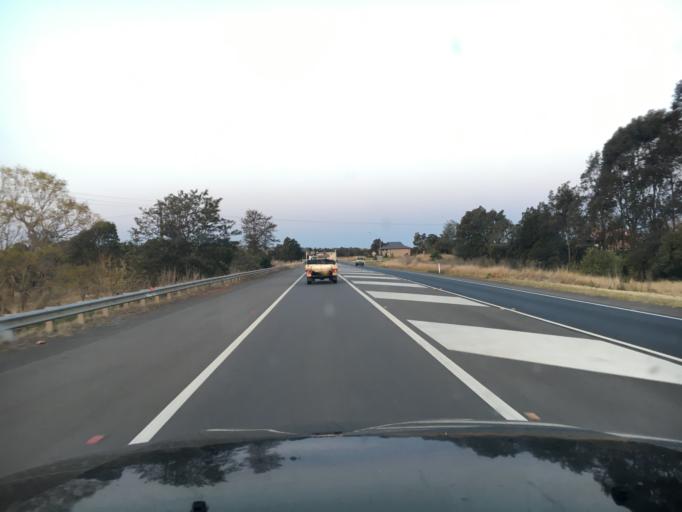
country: AU
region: New South Wales
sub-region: Cessnock
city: Greta
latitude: -32.7045
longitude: 151.4374
